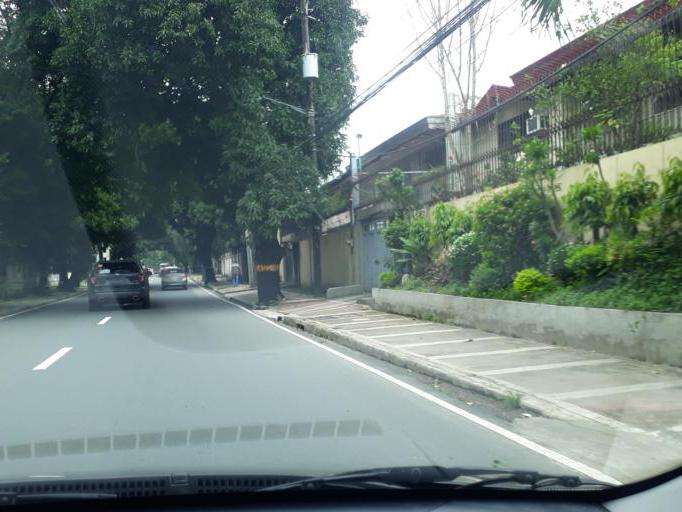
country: PH
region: Metro Manila
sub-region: San Juan
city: San Juan
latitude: 14.6192
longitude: 121.0314
